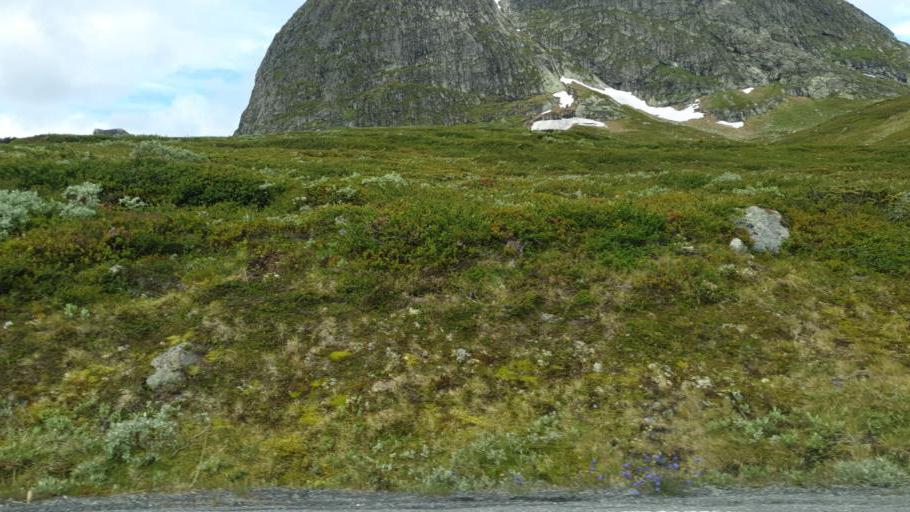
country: NO
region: Oppland
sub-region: Vestre Slidre
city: Slidre
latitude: 61.3363
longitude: 8.8127
